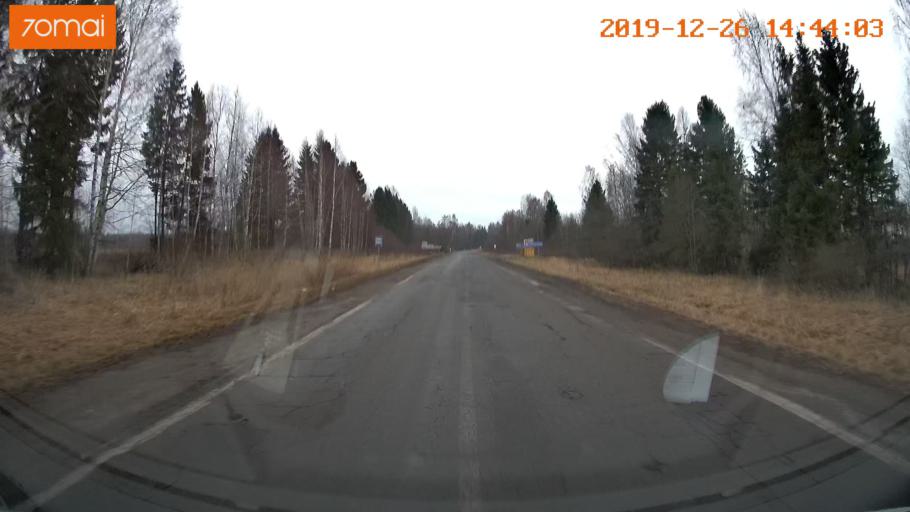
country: RU
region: Jaroslavl
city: Poshekhon'ye
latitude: 58.3514
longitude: 39.0468
